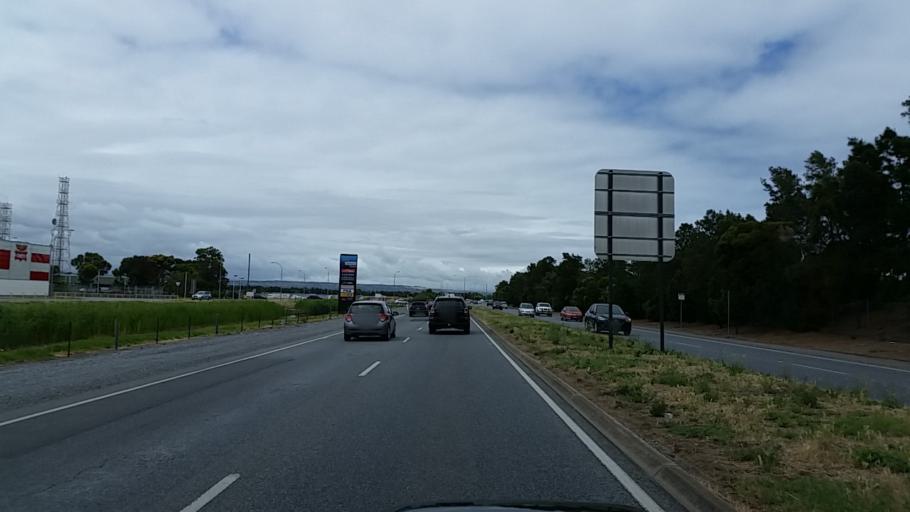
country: AU
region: South Australia
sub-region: Holdfast Bay
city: Glenelg East
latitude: -34.9479
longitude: 138.5180
